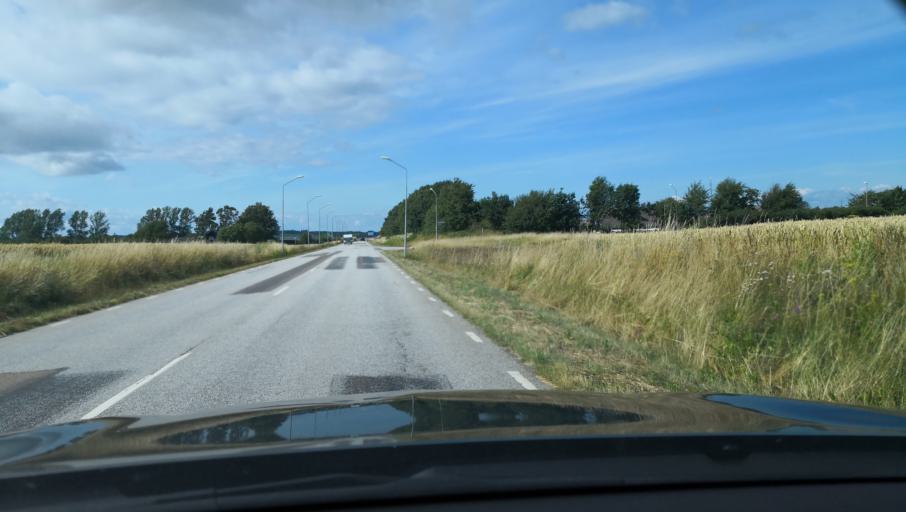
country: SE
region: Skane
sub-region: Simrishamns Kommun
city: Simrishamn
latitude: 55.5387
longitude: 14.3387
